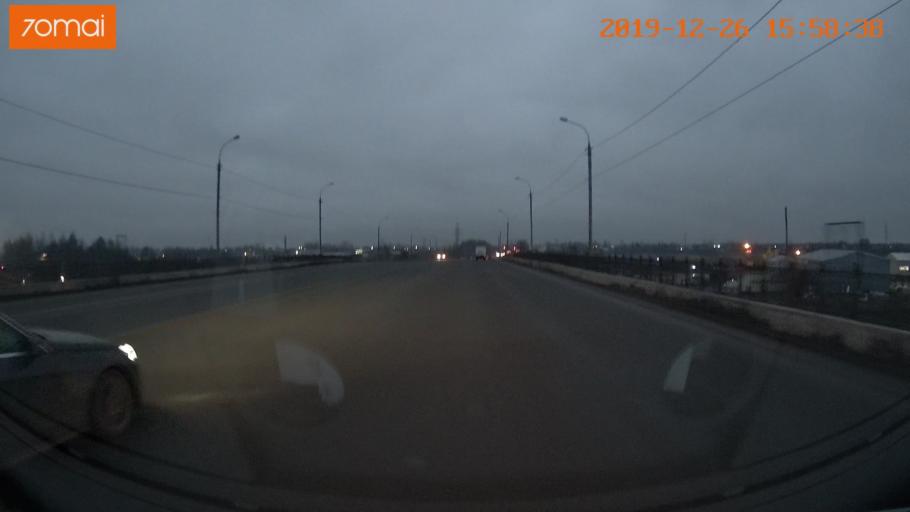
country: RU
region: Jaroslavl
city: Rybinsk
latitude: 58.0377
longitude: 38.7971
